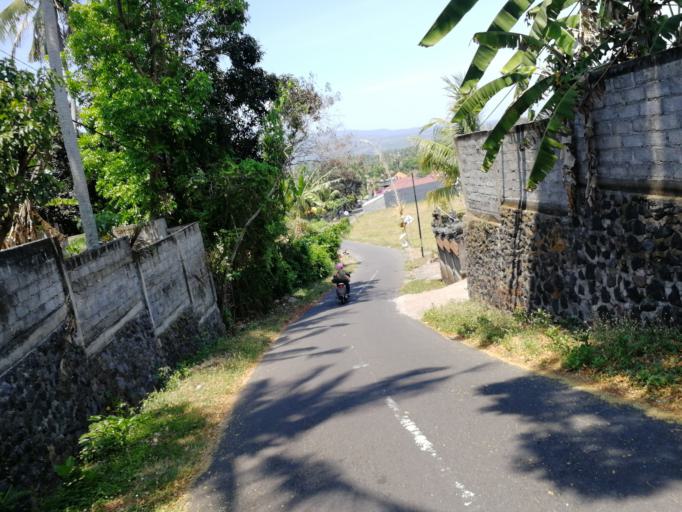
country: ID
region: Bali
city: Banjar Timbrah
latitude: -8.4672
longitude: 115.5918
